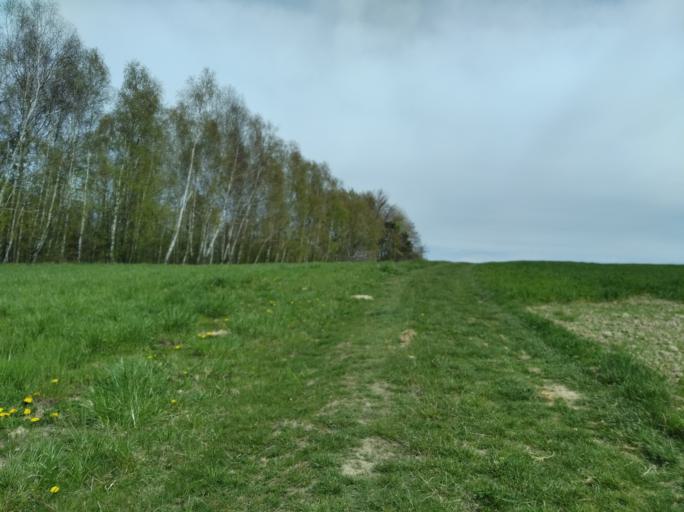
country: PL
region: Subcarpathian Voivodeship
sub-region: Powiat ropczycko-sedziszowski
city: Wielopole Skrzynskie
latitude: 49.9124
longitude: 21.6117
